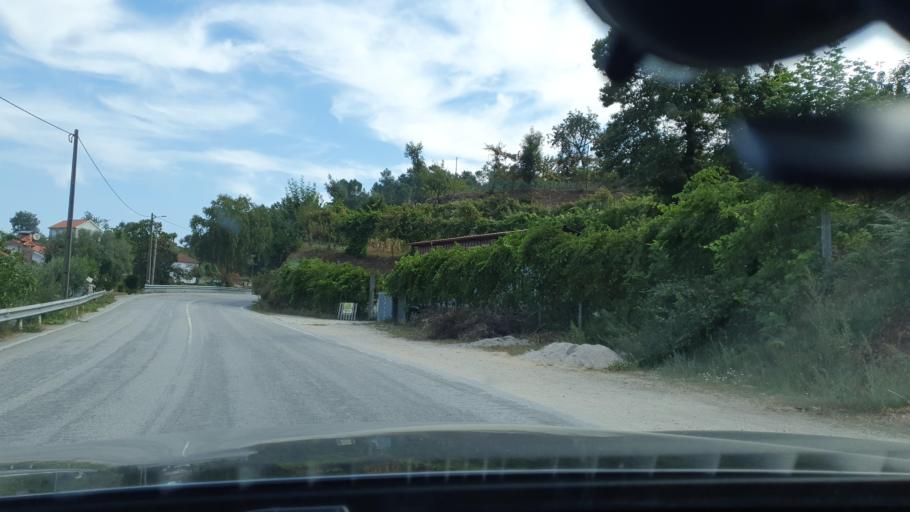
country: PT
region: Braga
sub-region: Vieira do Minho
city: Vieira do Minho
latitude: 41.6770
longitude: -8.1200
